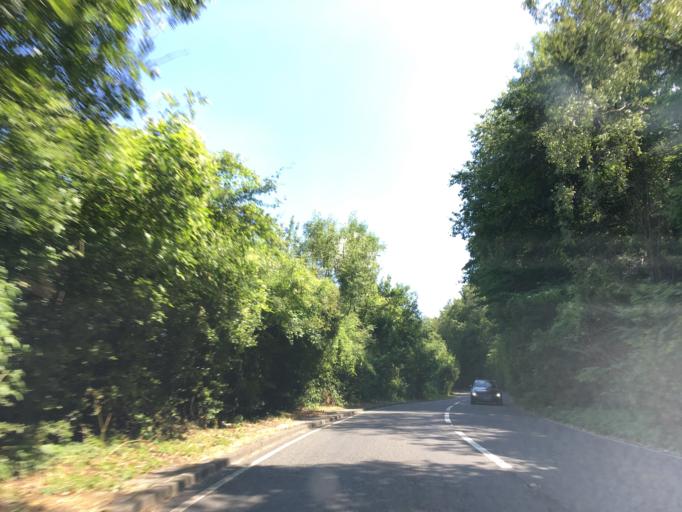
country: GB
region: England
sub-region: Gloucestershire
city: Chalford
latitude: 51.7203
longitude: -2.1478
